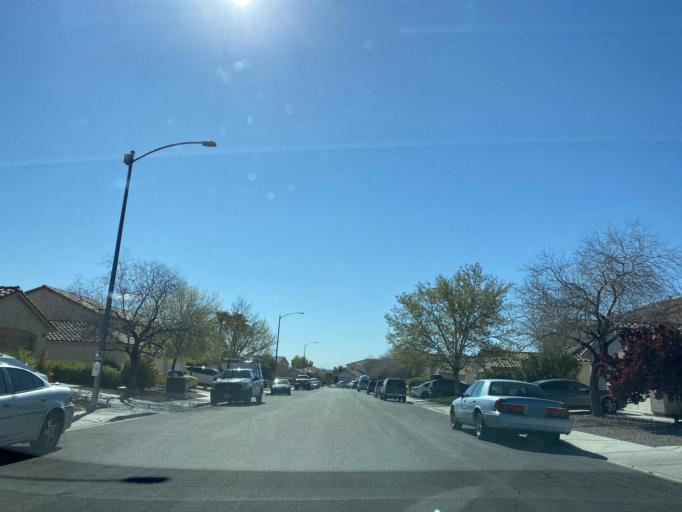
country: US
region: Nevada
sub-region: Clark County
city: Summerlin South
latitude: 36.3052
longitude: -115.2867
